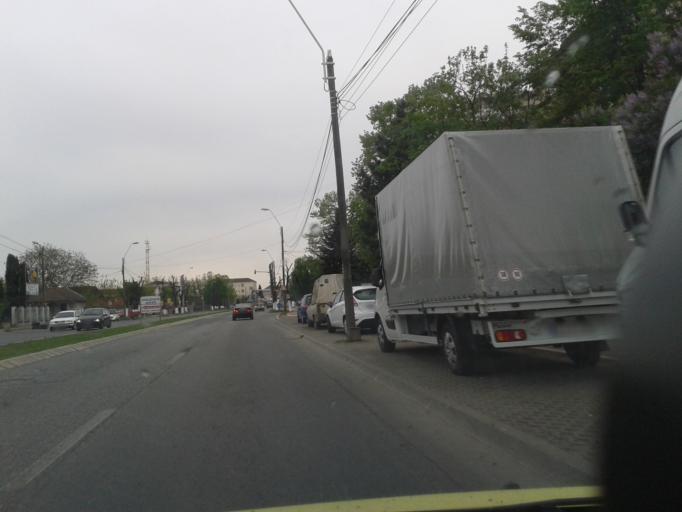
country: RO
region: Hunedoara
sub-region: Municipiul Deva
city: Deva
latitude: 45.8808
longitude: 22.9114
